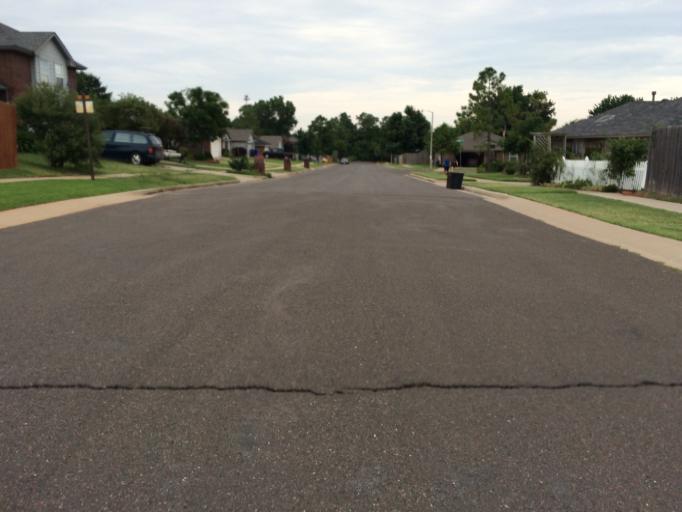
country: US
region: Oklahoma
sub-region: Cleveland County
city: Hall Park
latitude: 35.2548
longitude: -97.4308
